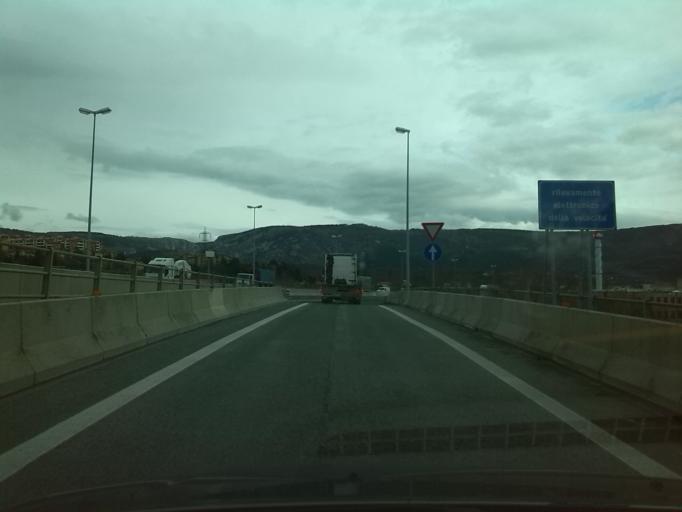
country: IT
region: Friuli Venezia Giulia
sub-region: Provincia di Trieste
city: Domio
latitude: 45.6163
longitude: 13.8177
